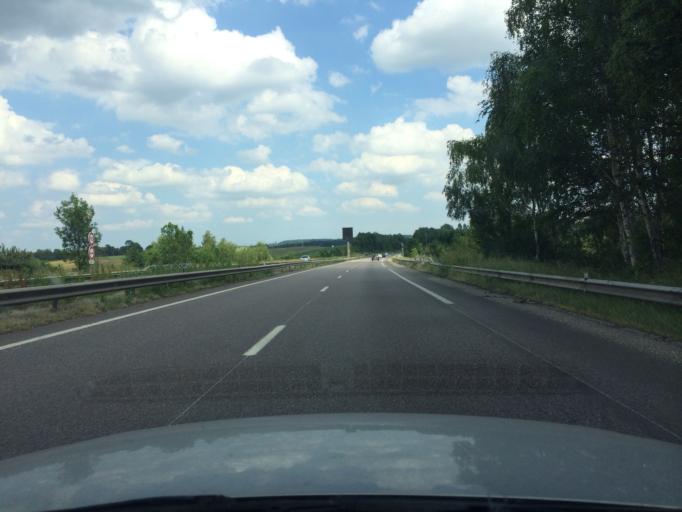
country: FR
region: Lorraine
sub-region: Departement de la Moselle
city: Phalsbourg
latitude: 48.7759
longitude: 7.2614
